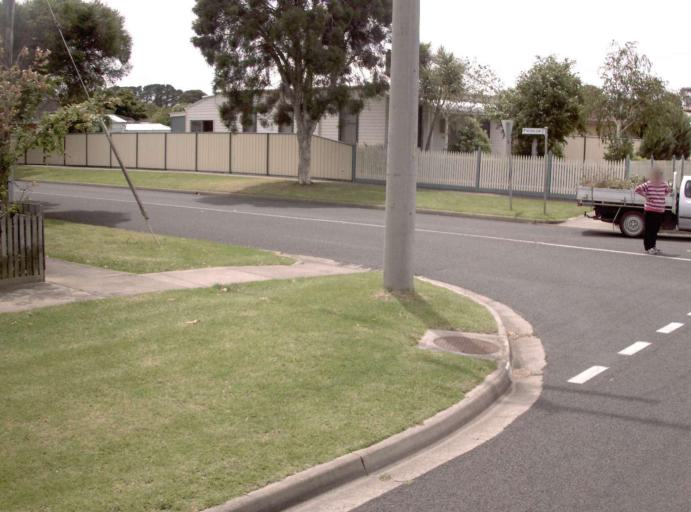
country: AU
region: Victoria
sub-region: Wellington
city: Sale
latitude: -38.0997
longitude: 147.0791
